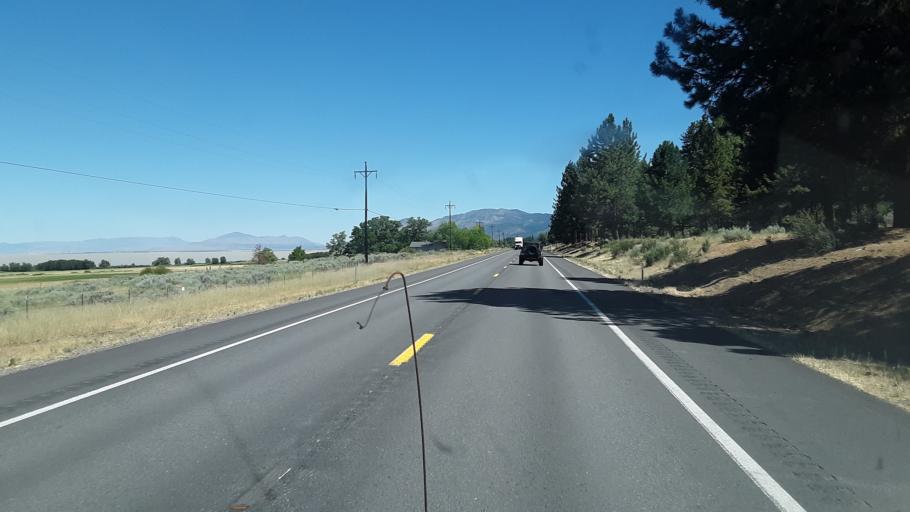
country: US
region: California
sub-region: Lassen County
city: Janesville
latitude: 40.2404
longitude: -120.4523
